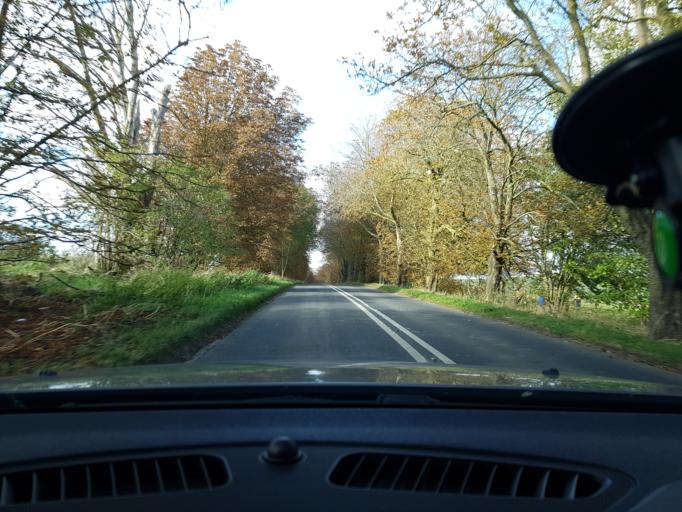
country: GB
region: England
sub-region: Borough of Swindon
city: Wanborough
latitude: 51.5111
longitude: -1.6764
